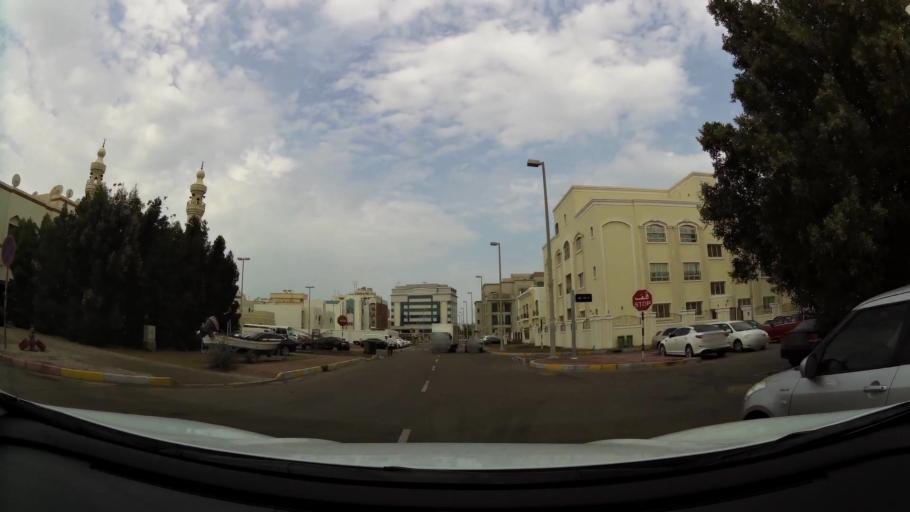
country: AE
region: Abu Dhabi
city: Abu Dhabi
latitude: 24.4441
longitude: 54.4077
